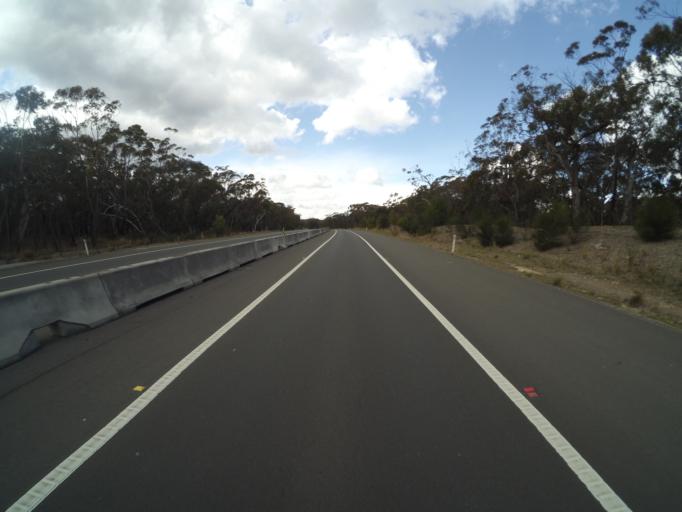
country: AU
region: New South Wales
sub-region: Wollongong
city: Mount Keira
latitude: -34.3313
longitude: 150.7781
